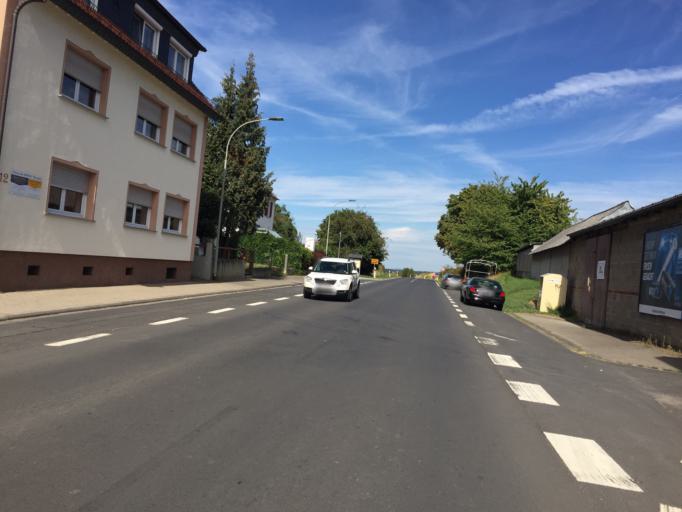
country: DE
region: Hesse
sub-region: Regierungsbezirk Giessen
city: Langgons
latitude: 50.4728
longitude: 8.6546
